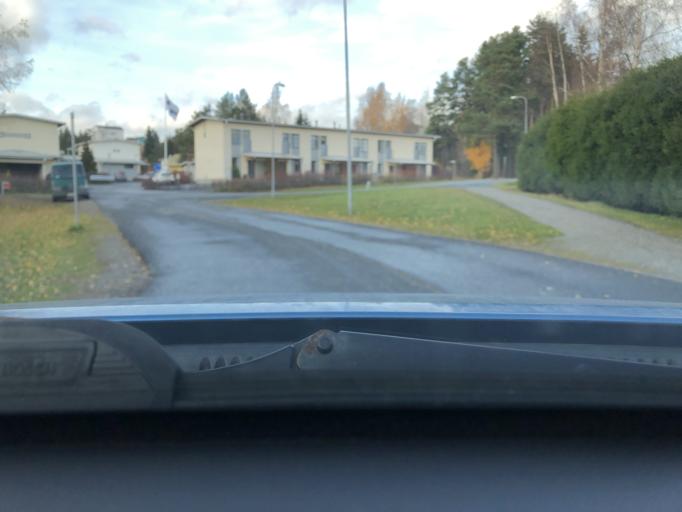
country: FI
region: Pirkanmaa
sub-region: Tampere
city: Kangasala
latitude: 61.4698
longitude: 24.0296
